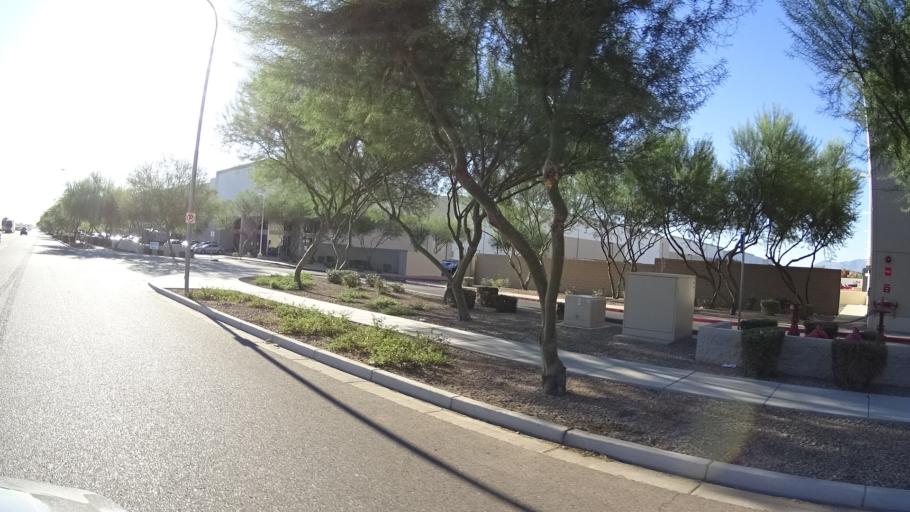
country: US
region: Arizona
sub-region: Maricopa County
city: Tolleson
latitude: 33.4304
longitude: -112.2203
